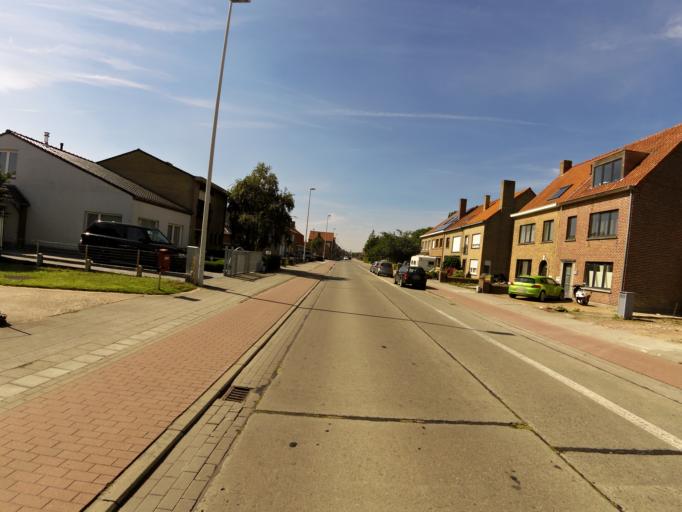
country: BE
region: Flanders
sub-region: Provincie West-Vlaanderen
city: Sint-Kruis
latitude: 51.2373
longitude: 3.2457
